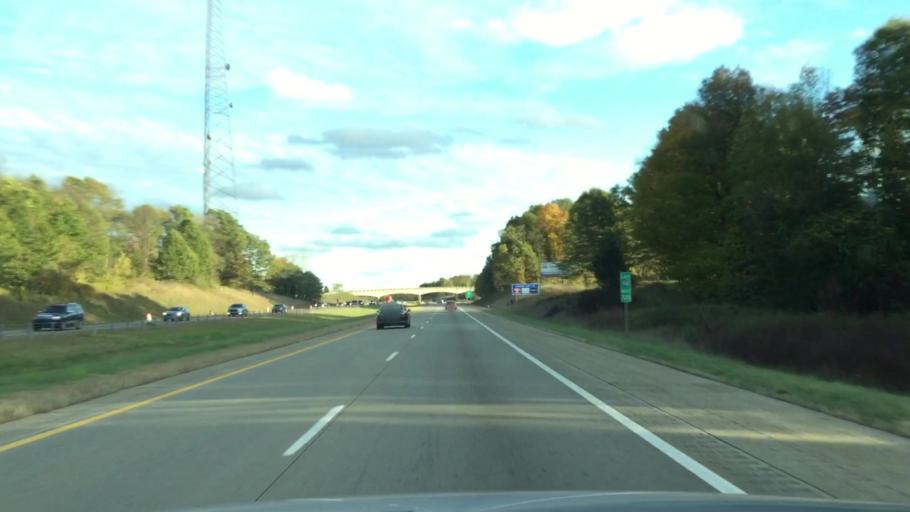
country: US
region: Michigan
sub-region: Calhoun County
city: Albion
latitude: 42.2716
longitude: -84.7803
